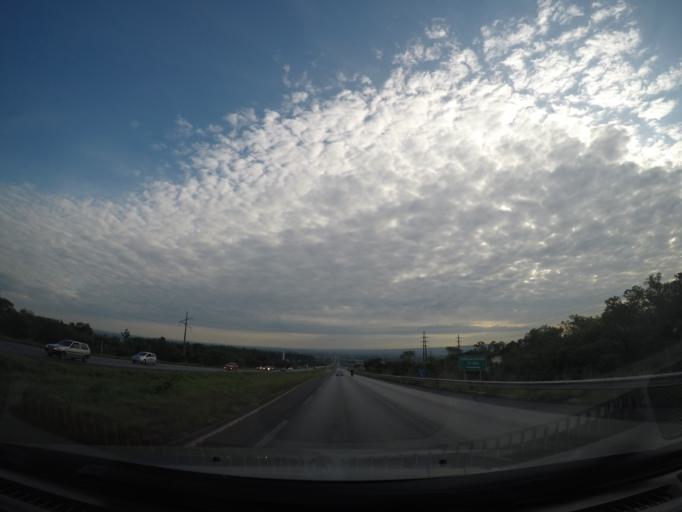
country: BR
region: Goias
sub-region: Planaltina
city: Planaltina
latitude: -15.6170
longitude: -47.7093
